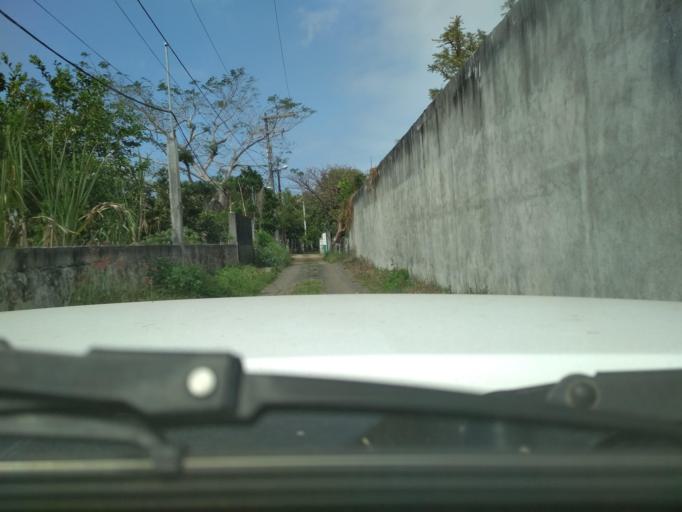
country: MX
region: Veracruz
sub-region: Veracruz
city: Delfino Victoria (Santa Fe)
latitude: 19.2522
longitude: -96.2641
